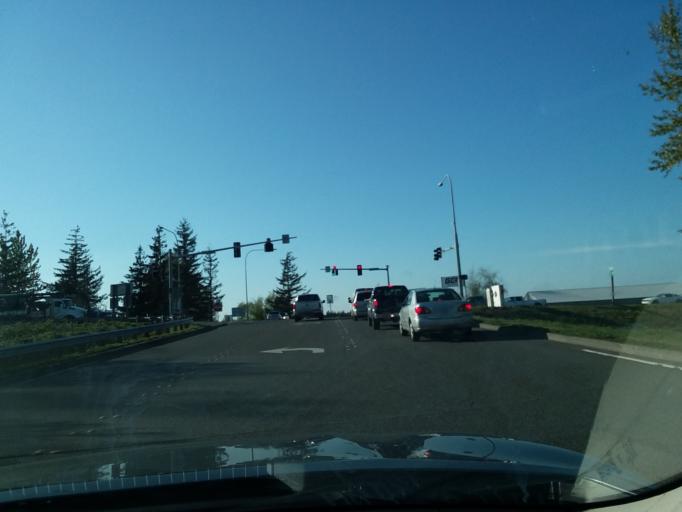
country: US
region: Washington
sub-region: Whatcom County
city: Ferndale
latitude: 48.8471
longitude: -122.5741
